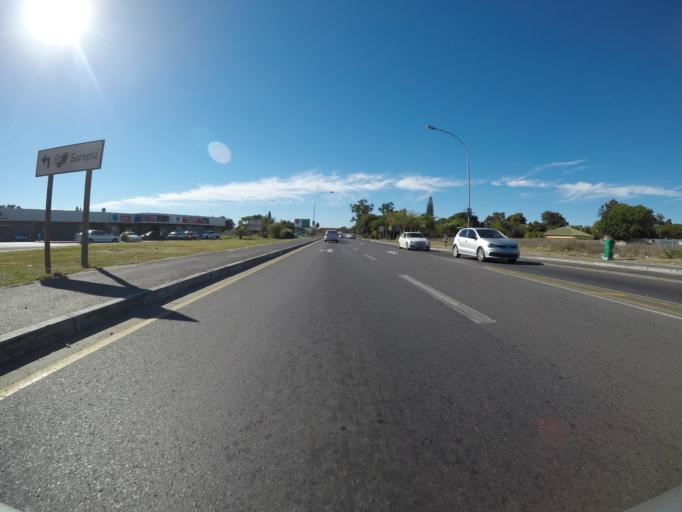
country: ZA
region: Western Cape
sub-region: City of Cape Town
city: Kraaifontein
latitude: -33.9353
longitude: 18.6766
